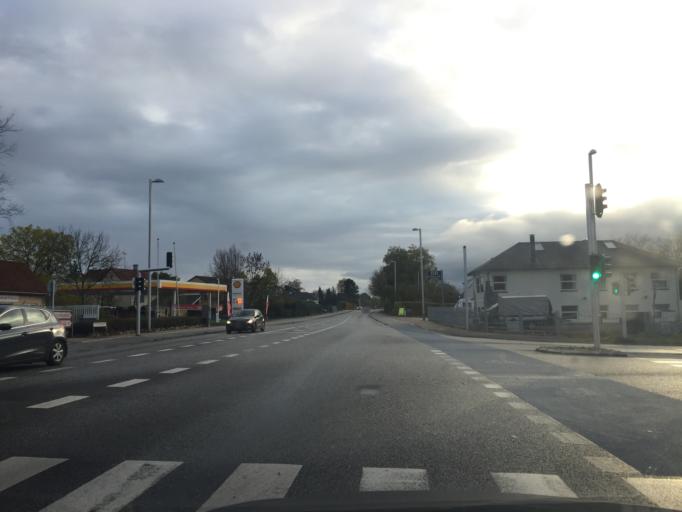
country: DK
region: Capital Region
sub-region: Fredensborg Kommune
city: Humlebaek
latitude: 55.9620
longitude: 12.5344
